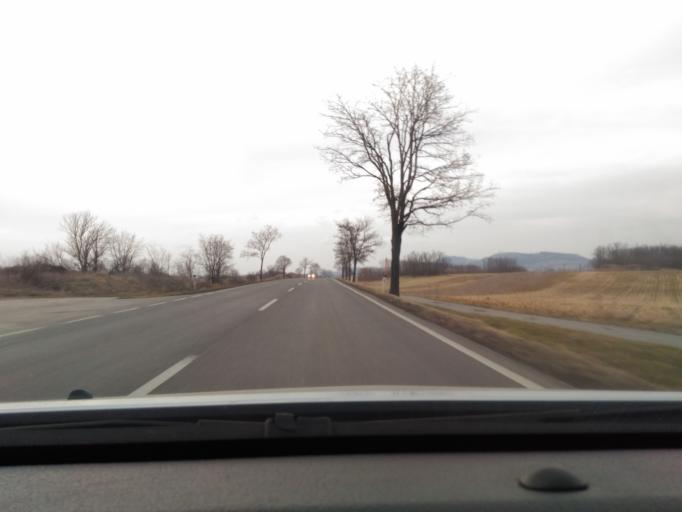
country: AT
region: Lower Austria
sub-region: Politischer Bezirk Mistelbach
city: Drasenhofen
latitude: 48.7657
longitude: 16.6450
